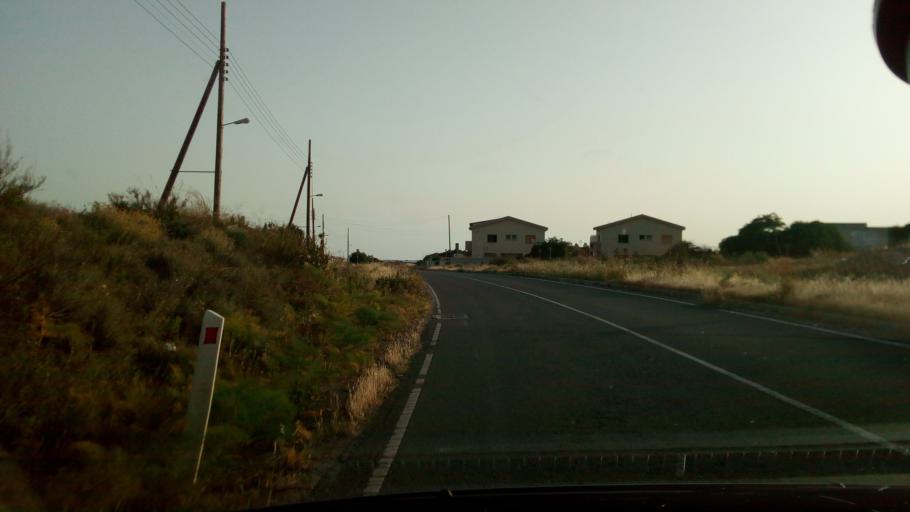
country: CY
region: Larnaka
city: Kofinou
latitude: 34.7690
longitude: 33.4420
